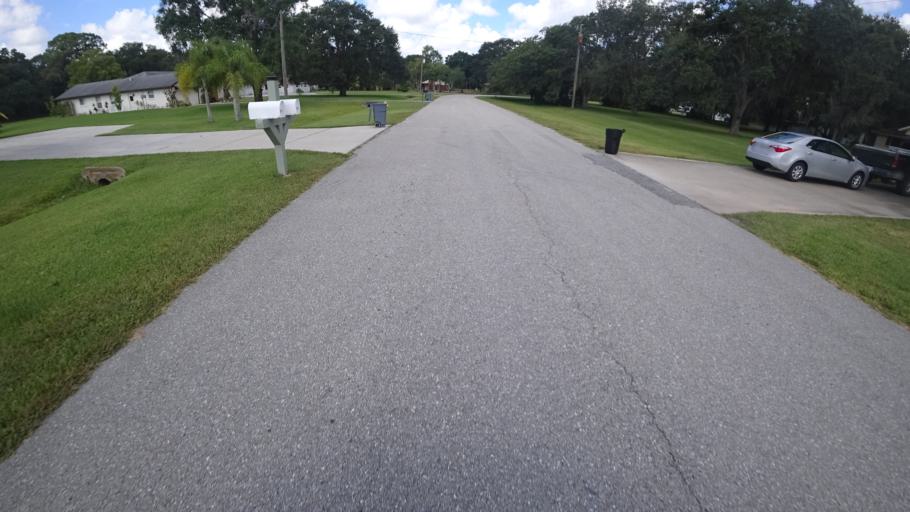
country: US
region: Florida
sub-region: Manatee County
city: Samoset
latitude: 27.4737
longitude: -82.4832
